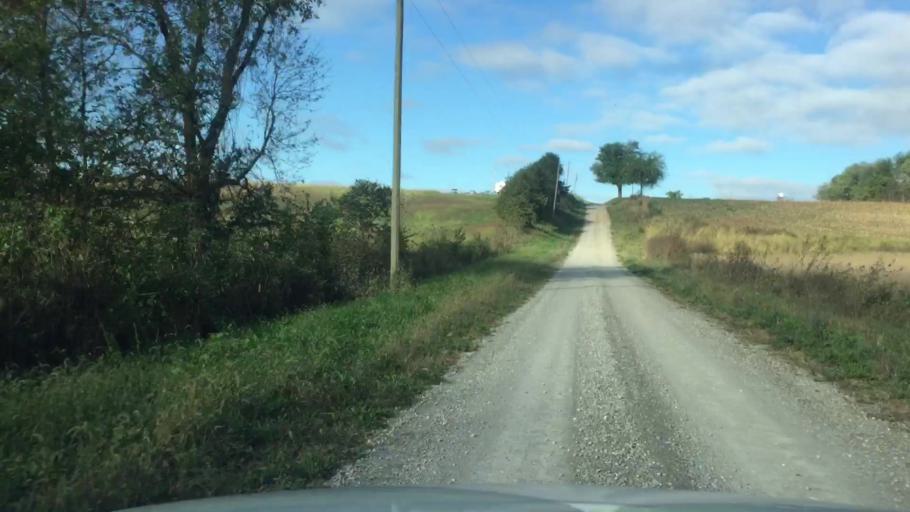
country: US
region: Missouri
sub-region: Howard County
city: New Franklin
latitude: 39.0833
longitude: -92.7713
